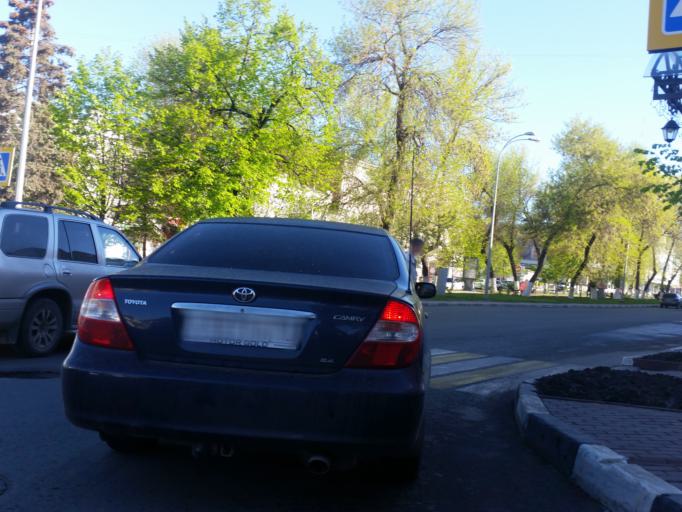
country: RU
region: Ulyanovsk
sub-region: Ulyanovskiy Rayon
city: Ulyanovsk
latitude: 54.3163
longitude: 48.3958
